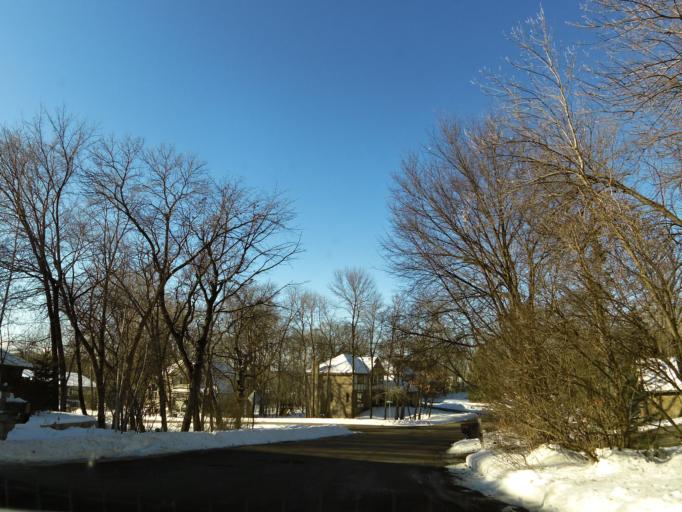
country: US
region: Minnesota
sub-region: Hennepin County
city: Edina
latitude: 44.8351
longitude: -93.3918
